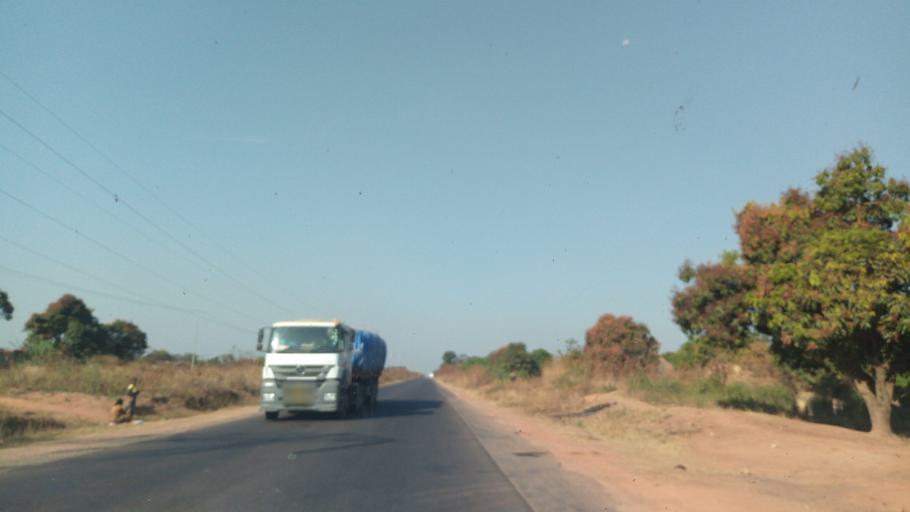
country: CD
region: Katanga
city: Likasi
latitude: -11.0021
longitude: 26.8594
